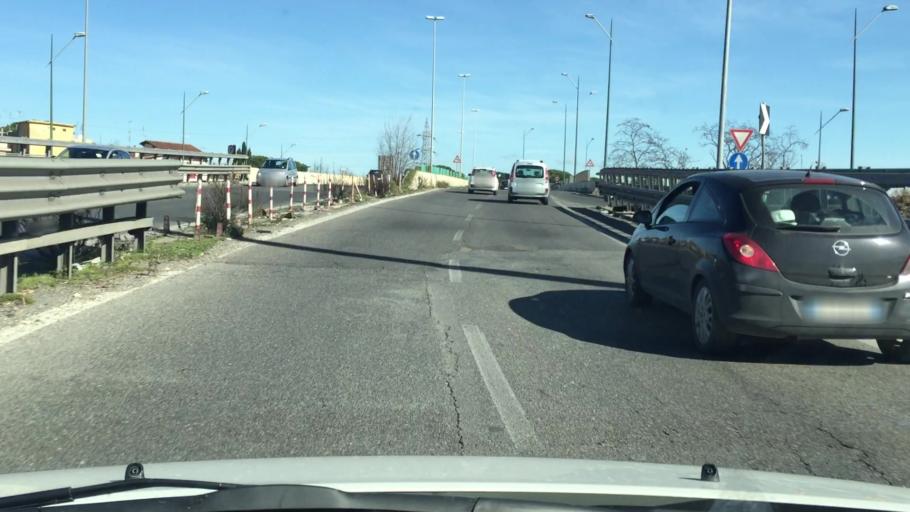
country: IT
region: Latium
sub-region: Citta metropolitana di Roma Capitale
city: Monte Caminetto
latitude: 41.9868
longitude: 12.4931
